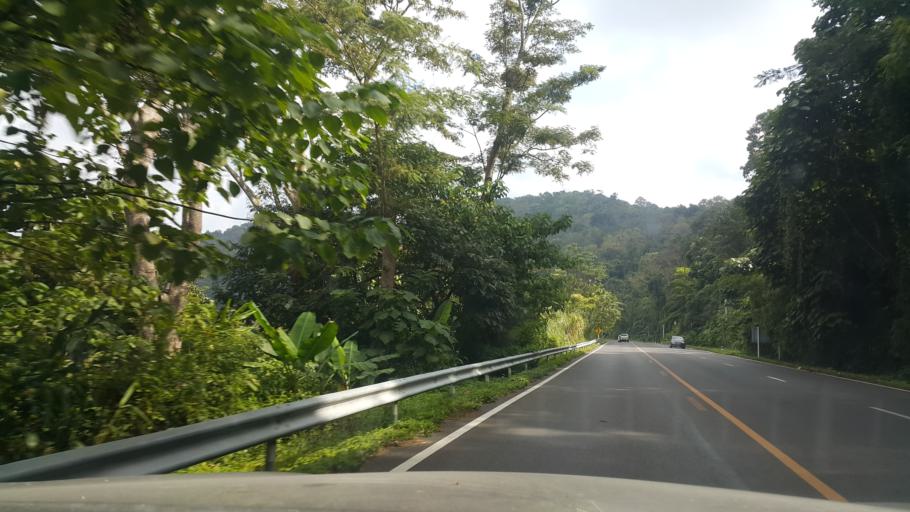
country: TH
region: Phayao
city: Phayao
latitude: 19.0592
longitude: 99.7845
